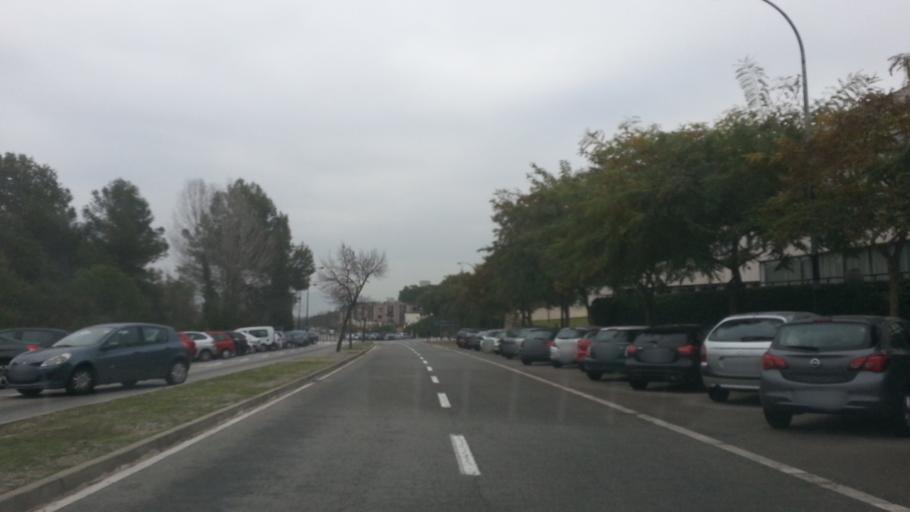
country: ES
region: Catalonia
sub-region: Provincia de Barcelona
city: Barbera del Valles
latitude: 41.5004
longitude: 2.0958
